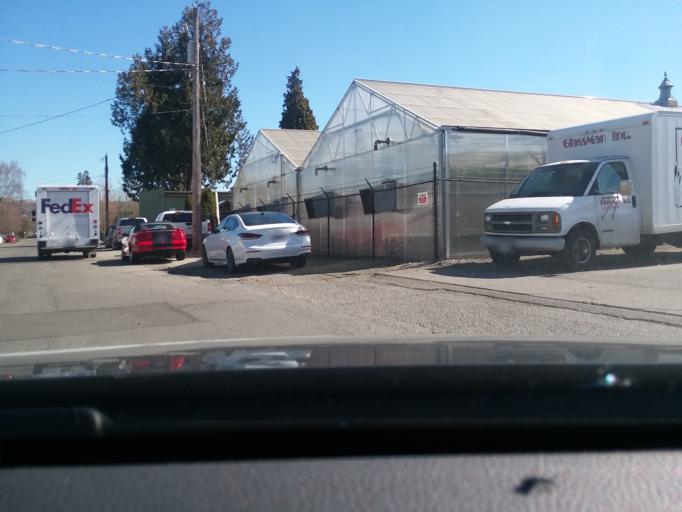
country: US
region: Washington
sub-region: Pierce County
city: Sumner
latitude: 47.2042
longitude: -122.2409
